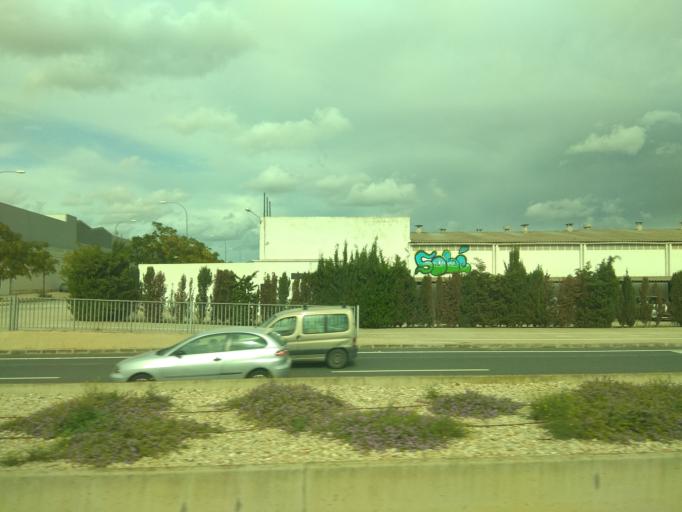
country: ES
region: Balearic Islands
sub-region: Illes Balears
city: Palma
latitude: 39.5703
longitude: 2.6887
